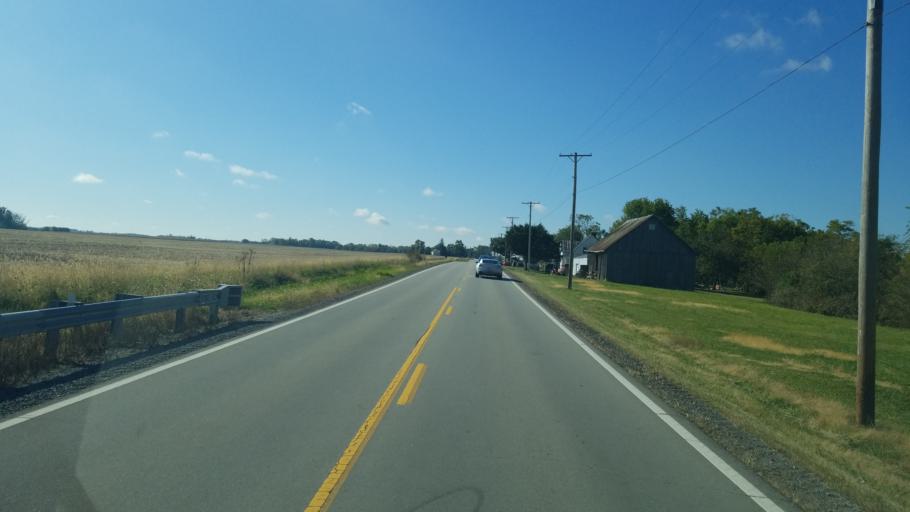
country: US
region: Ohio
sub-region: Fayette County
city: Washington Court House
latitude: 39.4703
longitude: -83.4855
